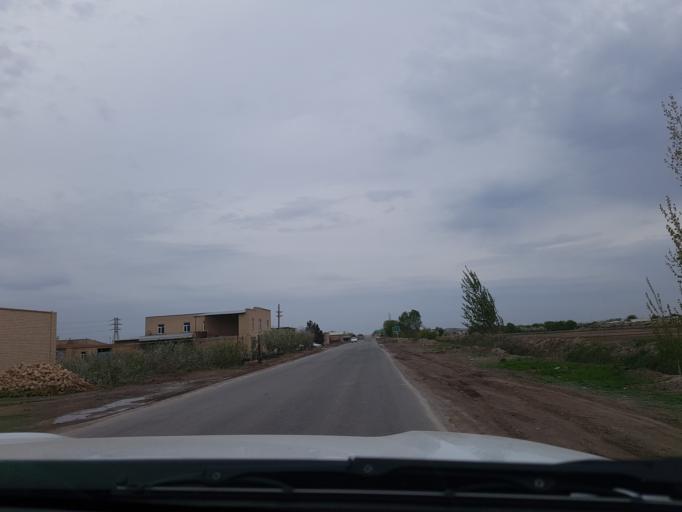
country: TM
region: Lebap
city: Turkmenabat
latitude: 39.0657
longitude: 63.5530
